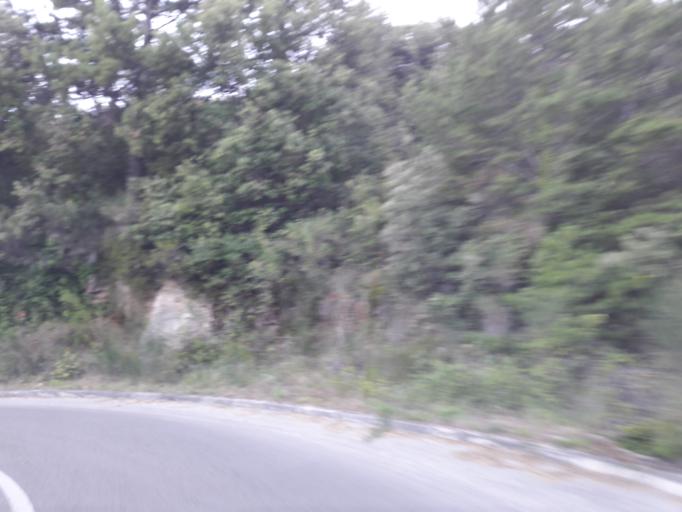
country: HR
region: Dubrovacko-Neretvanska
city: Orebic
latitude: 42.9964
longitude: 17.2633
